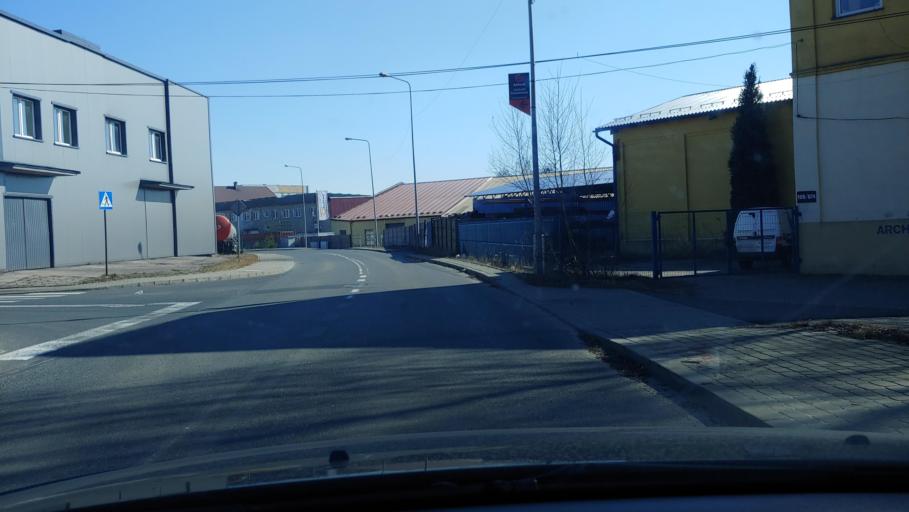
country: PL
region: Lesser Poland Voivodeship
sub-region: Powiat chrzanowski
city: Trzebinia
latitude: 50.1548
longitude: 19.4575
